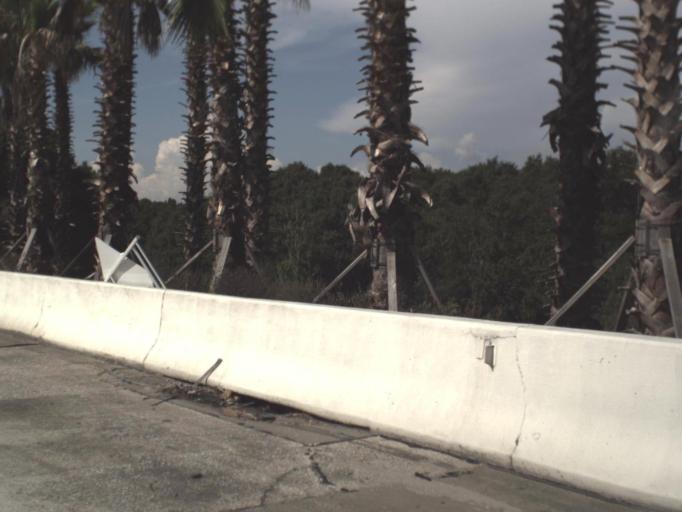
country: US
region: Florida
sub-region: Hillsborough County
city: Mango
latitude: 28.0054
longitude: -82.3277
